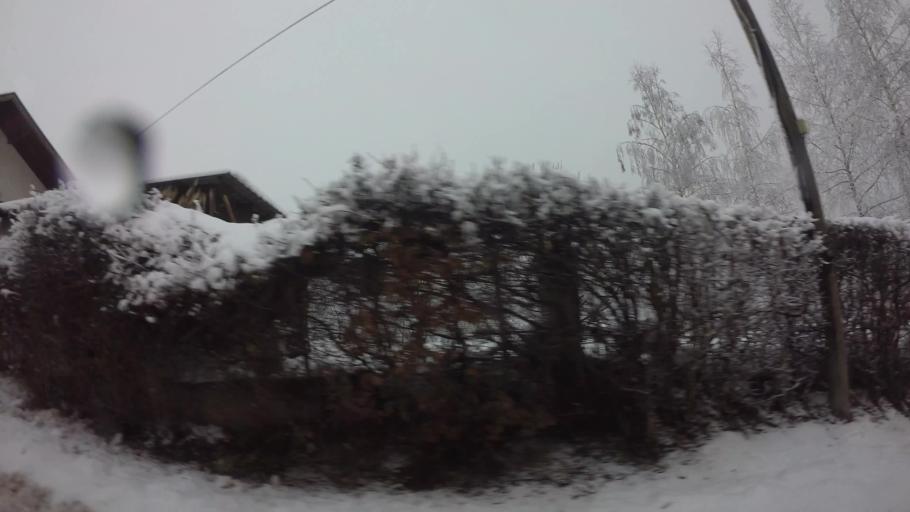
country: BA
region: Federation of Bosnia and Herzegovina
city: Vogosca
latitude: 43.8722
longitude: 18.3201
